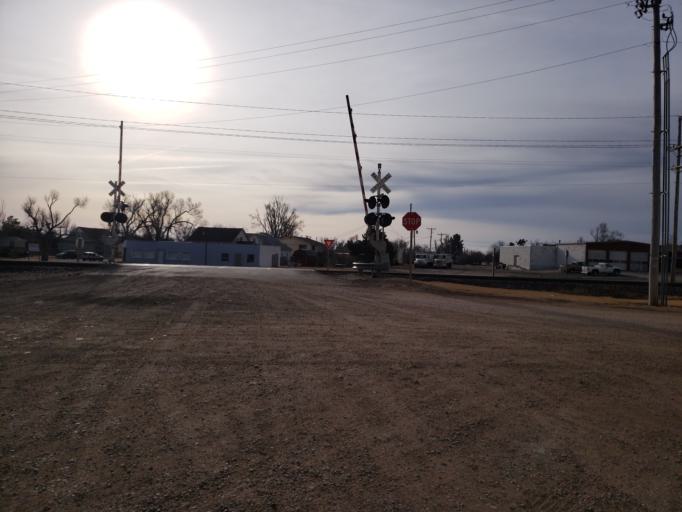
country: US
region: Kansas
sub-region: Ford County
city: Dodge City
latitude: 37.4437
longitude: -100.0188
